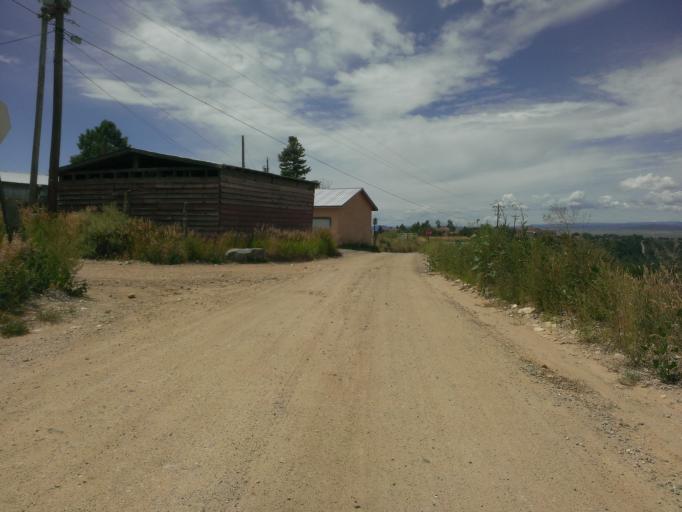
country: US
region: New Mexico
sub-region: Taos County
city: Arroyo Seco
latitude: 36.5334
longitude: -105.5657
